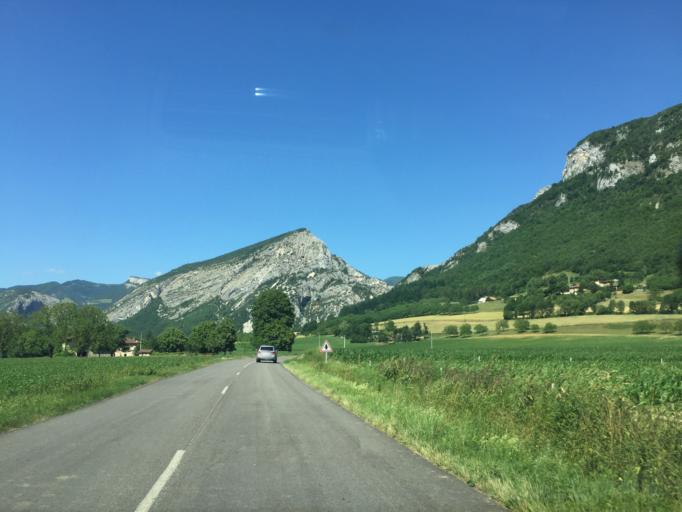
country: FR
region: Rhone-Alpes
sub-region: Departement de la Drome
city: Saint-Laurent-en-Royans
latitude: 45.0374
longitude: 5.3338
